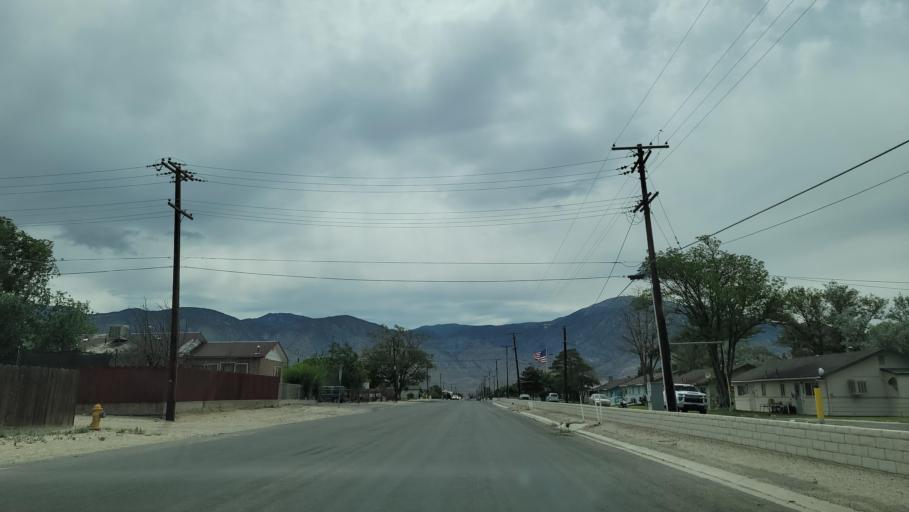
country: US
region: Nevada
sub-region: Mineral County
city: Hawthorne
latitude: 38.5324
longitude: -118.6201
